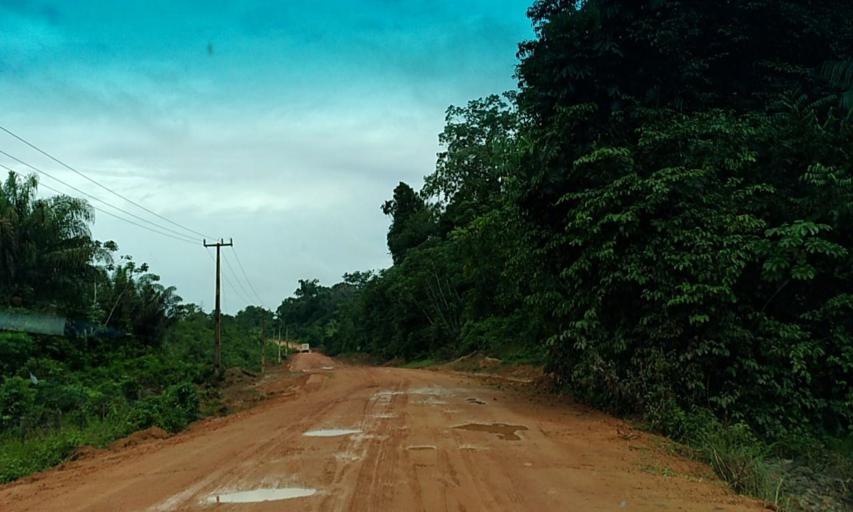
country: BR
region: Para
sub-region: Senador Jose Porfirio
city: Senador Jose Porfirio
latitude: -3.0169
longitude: -51.6811
